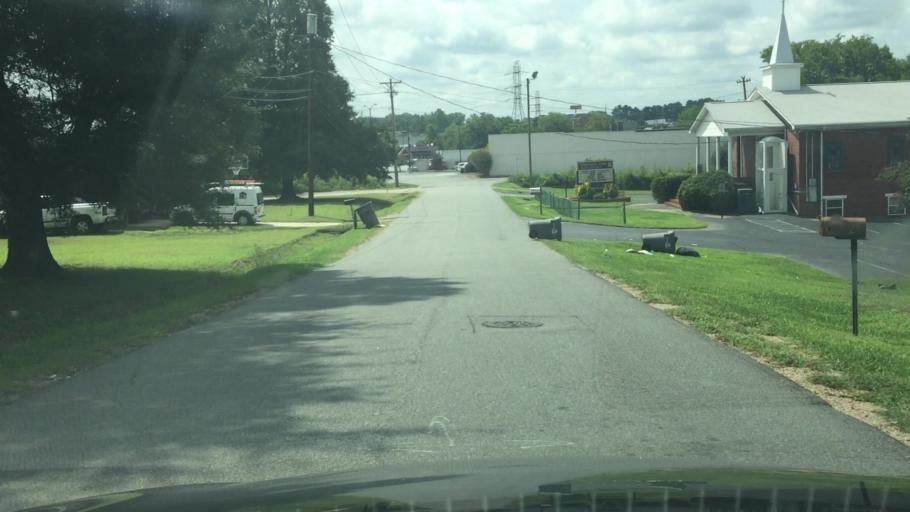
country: US
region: North Carolina
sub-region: Cabarrus County
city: Kannapolis
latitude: 35.4527
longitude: -80.6072
